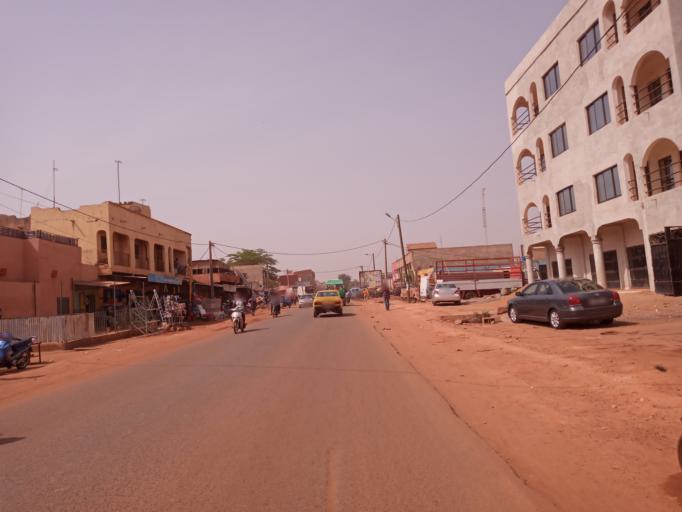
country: ML
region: Bamako
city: Bamako
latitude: 12.5915
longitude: -7.9643
